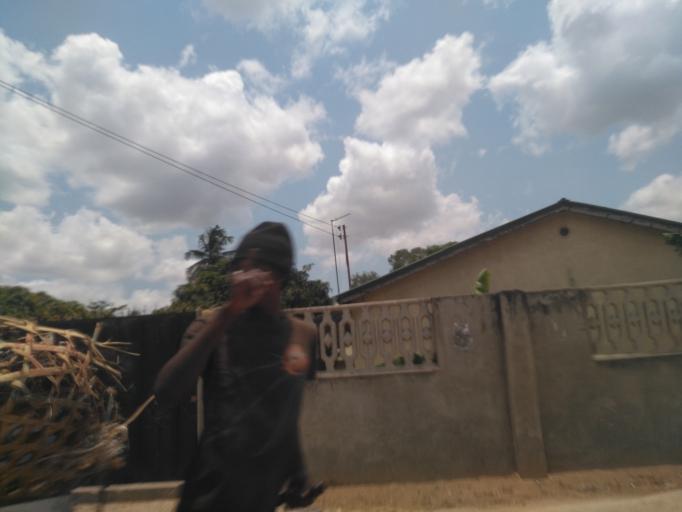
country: TZ
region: Dar es Salaam
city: Dar es Salaam
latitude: -6.8367
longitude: 39.3175
